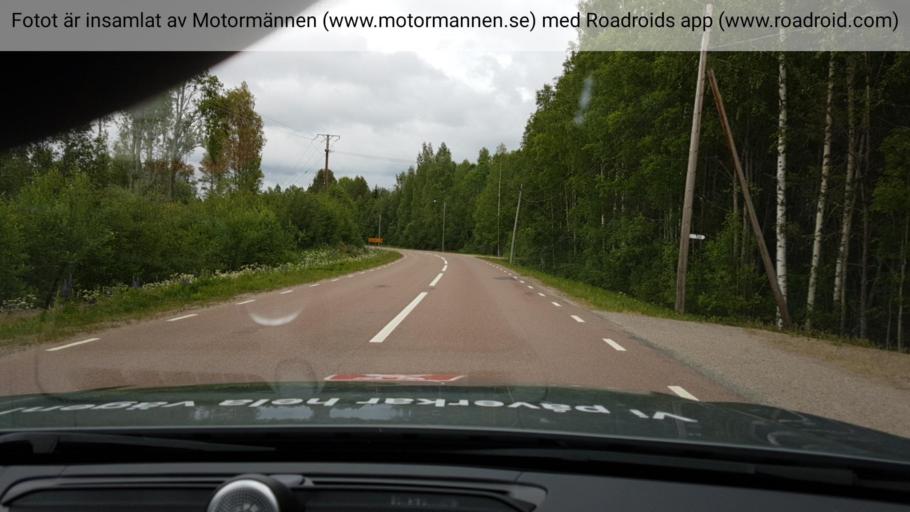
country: SE
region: Jaemtland
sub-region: Braecke Kommun
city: Braecke
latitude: 62.9047
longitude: 15.6692
